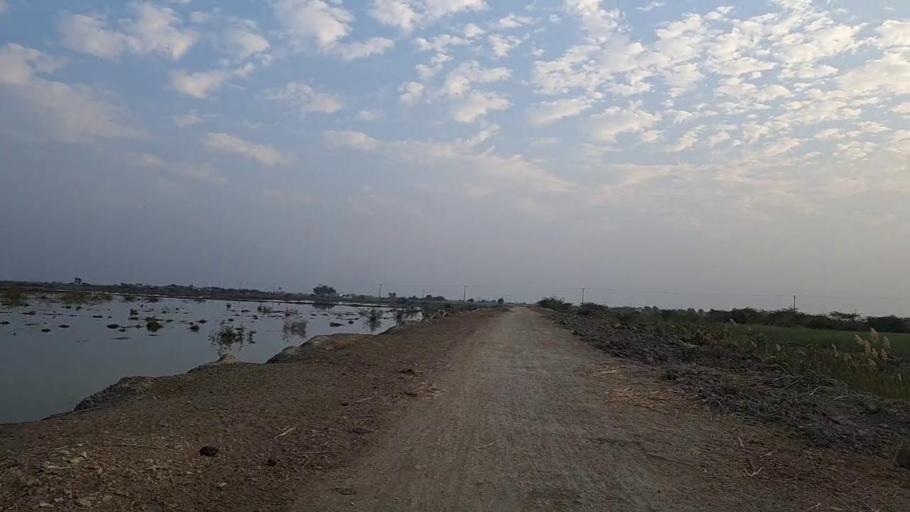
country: PK
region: Sindh
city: Pithoro
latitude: 25.4430
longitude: 69.3450
